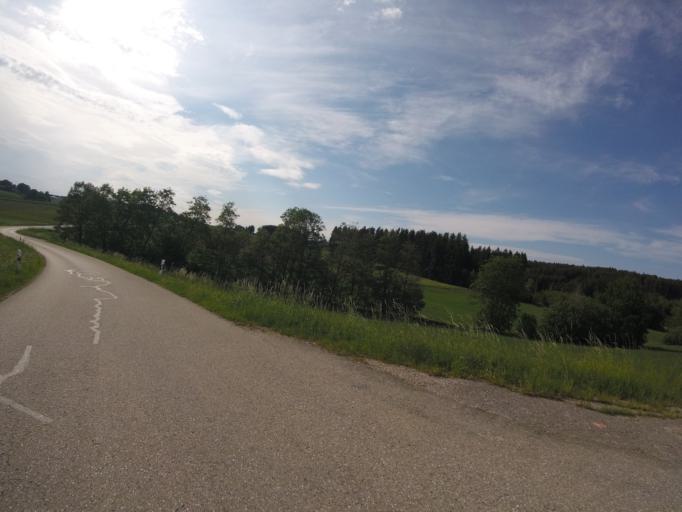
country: DE
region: Bavaria
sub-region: Upper Bavaria
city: Scheyern
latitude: 48.4712
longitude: 11.4648
